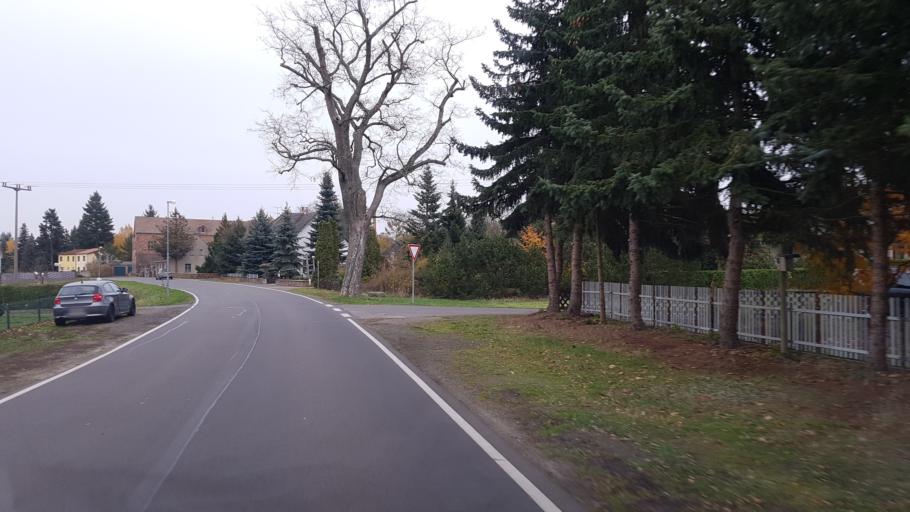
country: DE
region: Brandenburg
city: Crinitz
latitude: 51.7372
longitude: 13.7530
